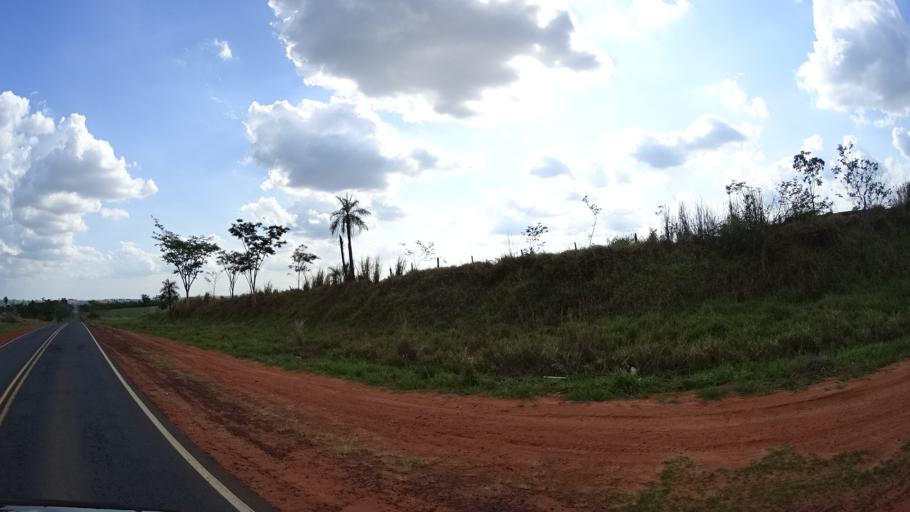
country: BR
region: Sao Paulo
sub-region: Urupes
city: Urupes
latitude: -21.1075
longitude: -49.2655
